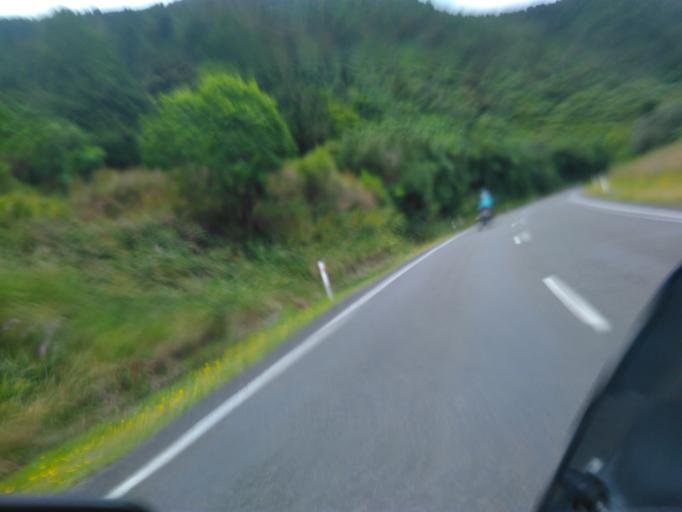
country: NZ
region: Bay of Plenty
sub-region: Opotiki District
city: Opotiki
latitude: -38.2923
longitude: 177.3890
